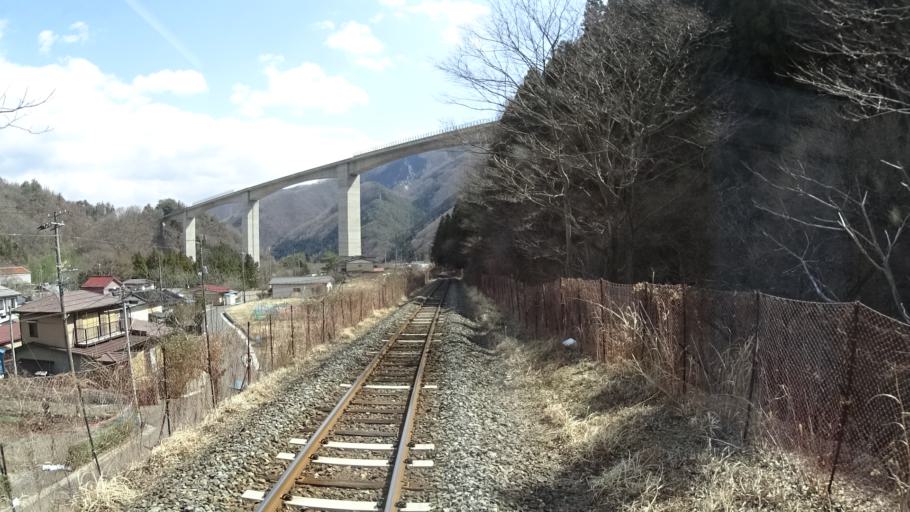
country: JP
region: Iwate
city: Kamaishi
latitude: 39.2532
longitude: 141.7522
